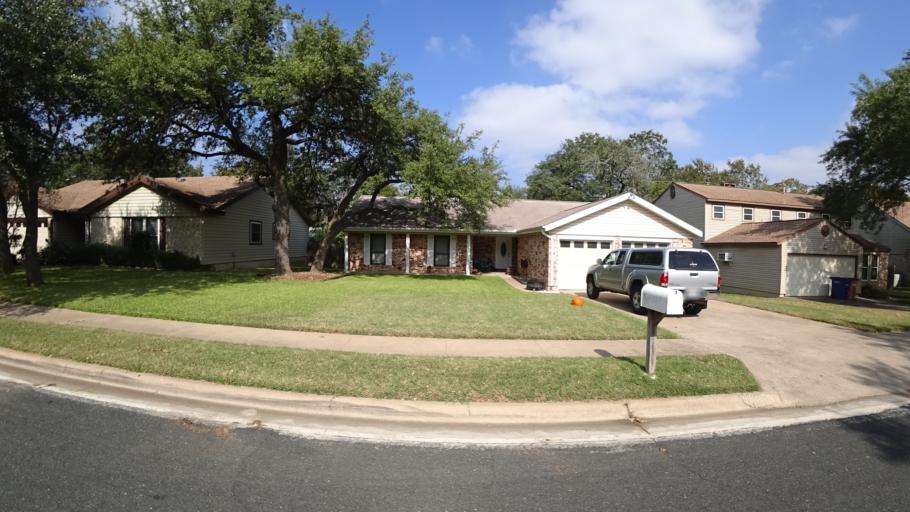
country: US
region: Texas
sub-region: Travis County
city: Shady Hollow
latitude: 30.2011
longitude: -97.8198
